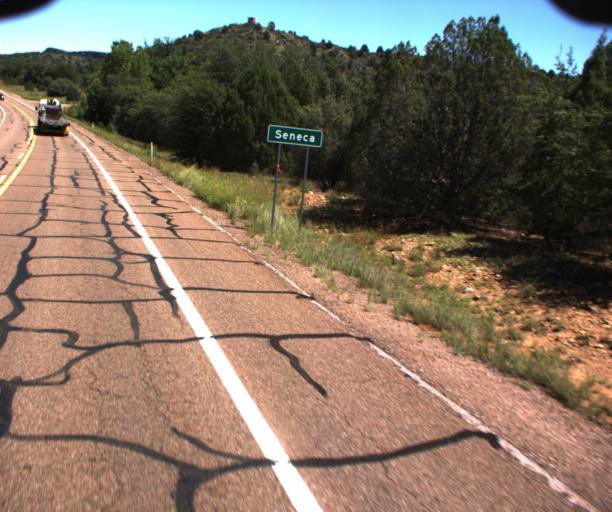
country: US
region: Arizona
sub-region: Navajo County
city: Cibecue
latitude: 33.7556
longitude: -110.5151
